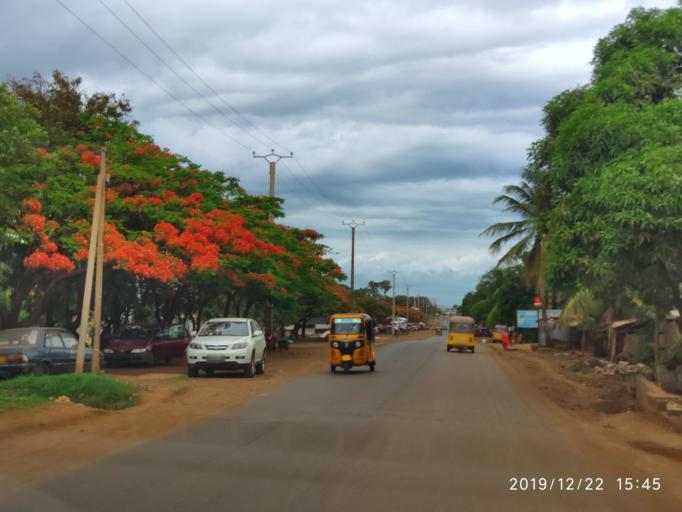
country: MG
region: Diana
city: Antsiranana
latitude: -12.3032
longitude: 49.2939
